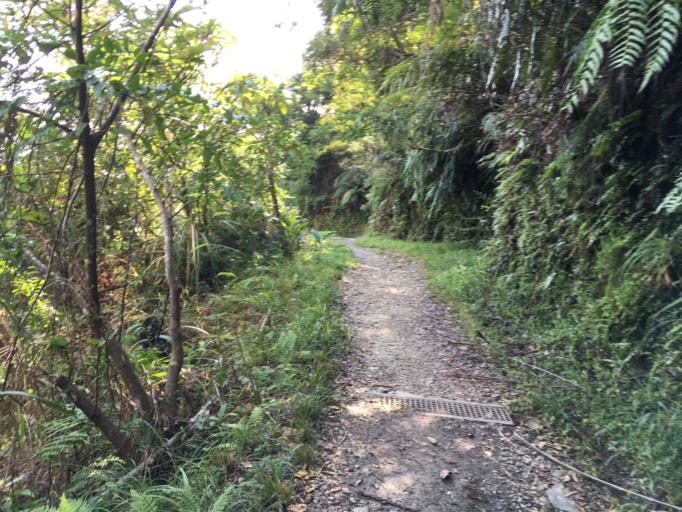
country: TW
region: Taiwan
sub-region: Yilan
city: Yilan
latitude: 24.8461
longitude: 121.7764
